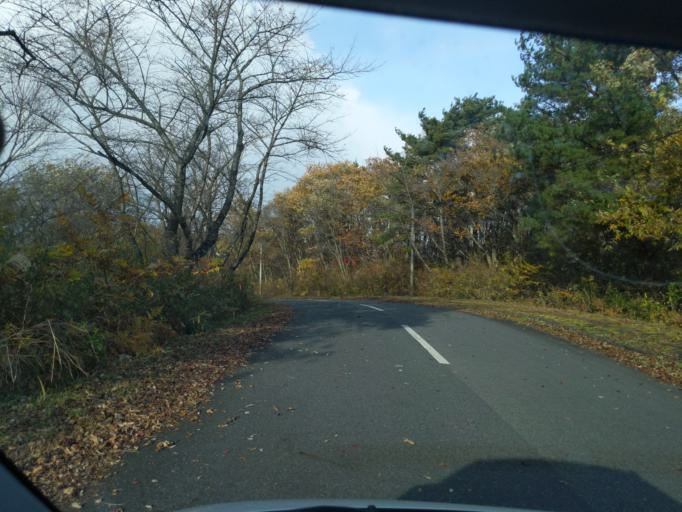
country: JP
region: Iwate
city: Mizusawa
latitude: 39.0257
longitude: 141.0930
